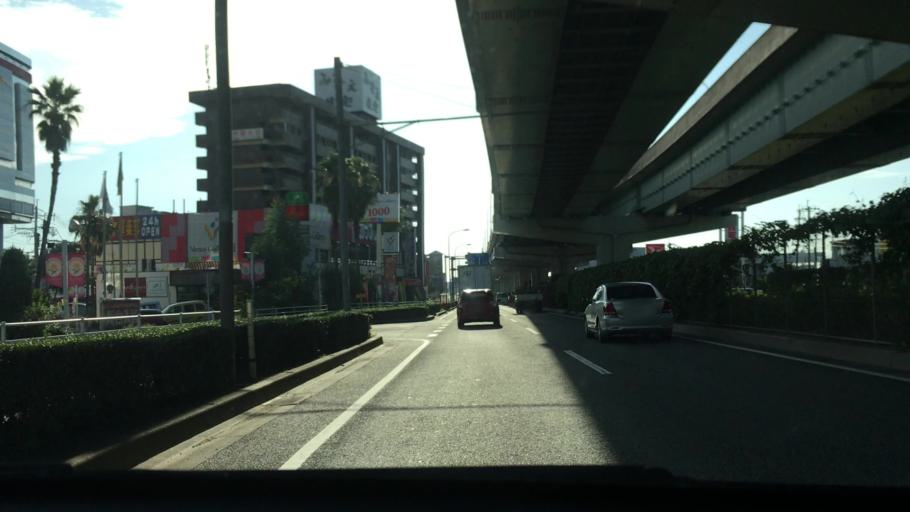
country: JP
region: Fukuoka
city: Fukuoka-shi
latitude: 33.6290
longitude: 130.4459
